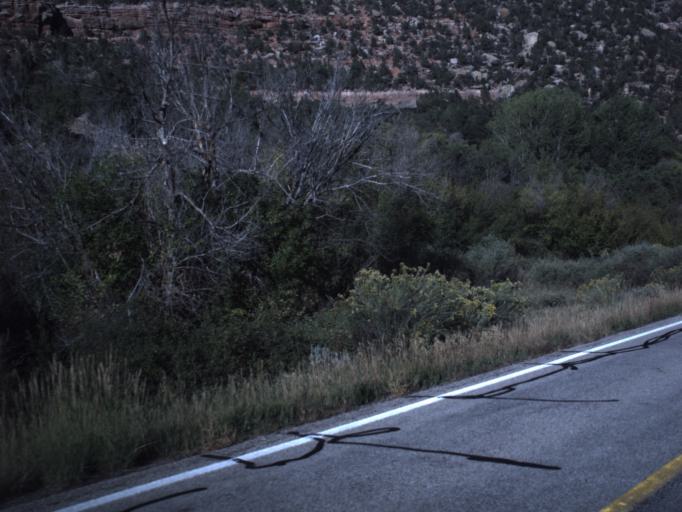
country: US
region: Utah
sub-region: Grand County
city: Moab
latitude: 38.3304
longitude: -109.0839
